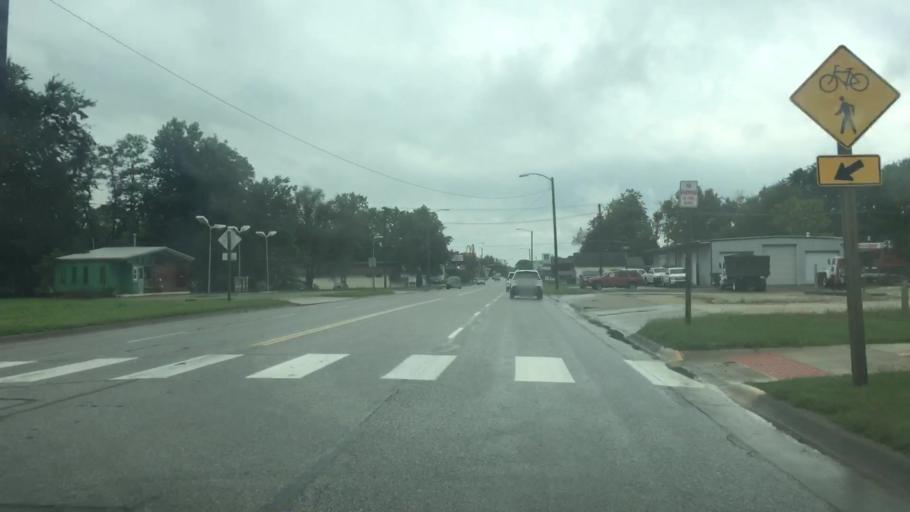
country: US
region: Kansas
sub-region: Allen County
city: Iola
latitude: 37.9257
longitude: -95.4091
